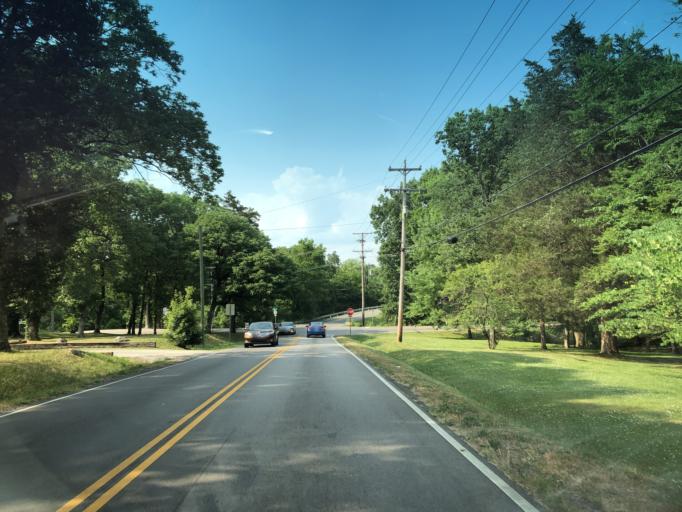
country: US
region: Tennessee
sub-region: Davidson County
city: Goodlettsville
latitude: 36.2759
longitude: -86.7296
